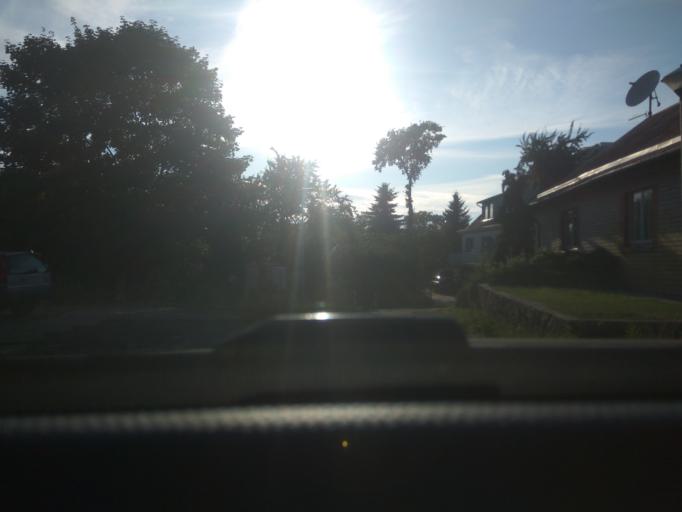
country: LV
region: Grobina
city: Grobina
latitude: 56.5313
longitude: 21.1750
